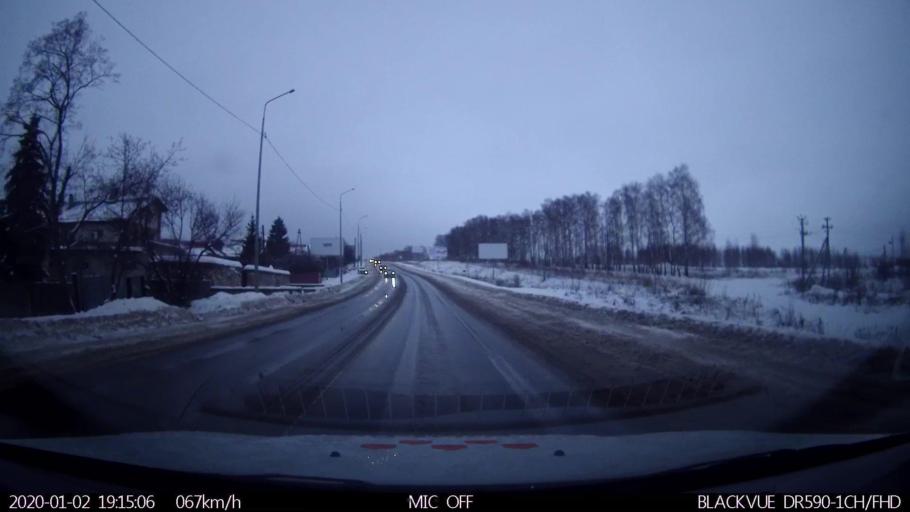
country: RU
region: Nizjnij Novgorod
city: Burevestnik
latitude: 56.2083
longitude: 43.8776
